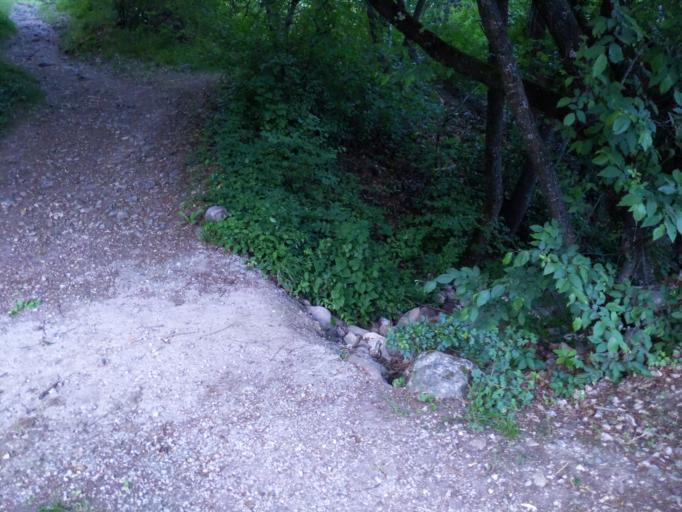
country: IT
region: Trentino-Alto Adige
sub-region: Bolzano
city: Caldaro sulla Strada del Vino
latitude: 46.4245
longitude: 11.2402
